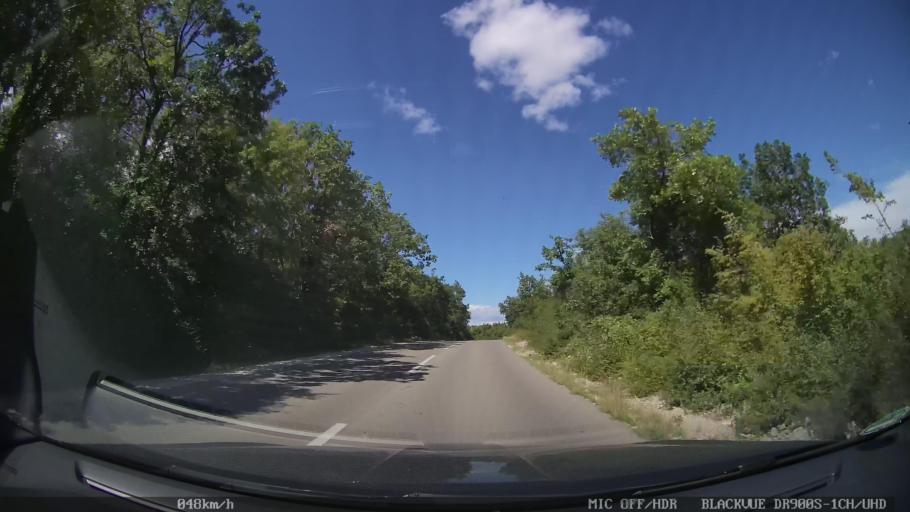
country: HR
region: Primorsko-Goranska
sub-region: Grad Krk
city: Krk
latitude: 45.0475
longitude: 14.5099
